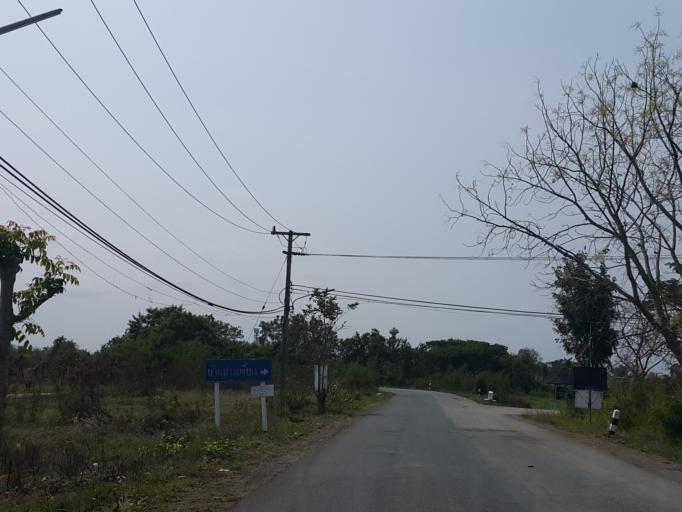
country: TH
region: Lamphun
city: Ban Thi
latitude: 18.6707
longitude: 99.0989
